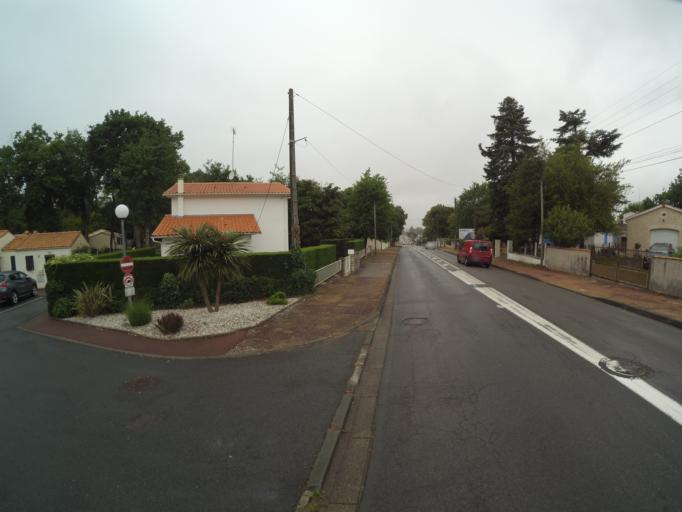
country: FR
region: Poitou-Charentes
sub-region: Departement de la Charente-Maritime
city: Saint-Georges-de-Didonne
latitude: 45.6115
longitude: -0.9974
